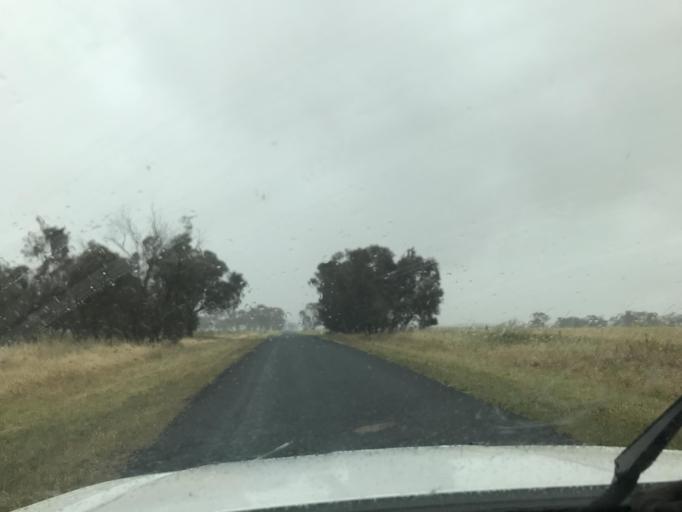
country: AU
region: South Australia
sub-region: Tatiara
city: Bordertown
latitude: -36.3161
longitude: 141.1733
